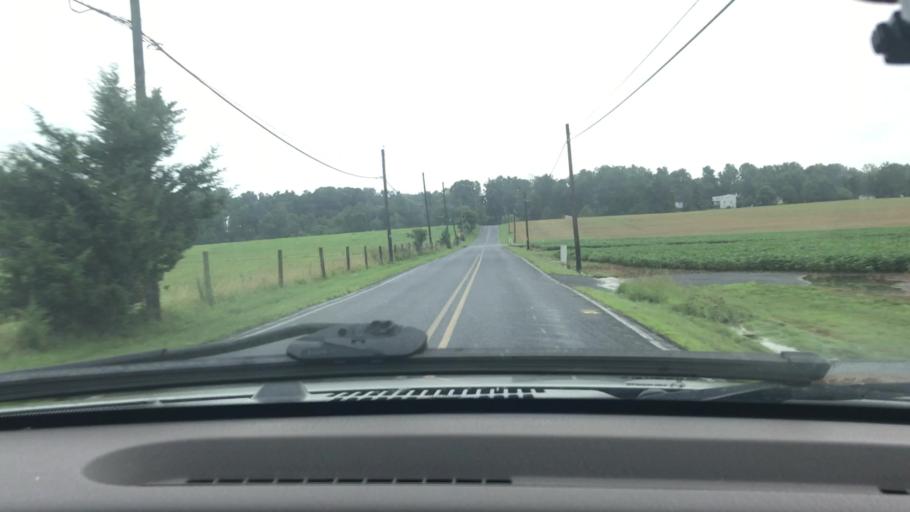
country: US
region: Pennsylvania
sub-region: Lancaster County
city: Elizabethtown
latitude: 40.2185
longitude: -76.6249
